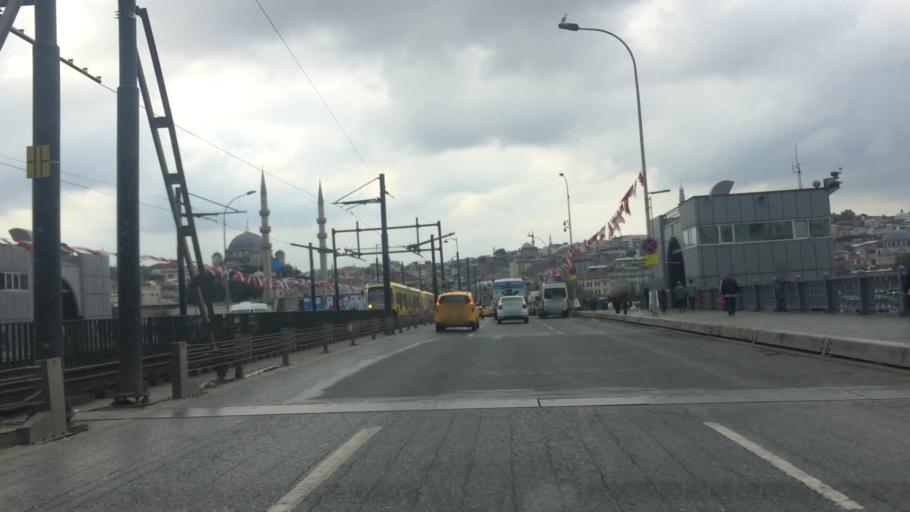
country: TR
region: Istanbul
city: Eminoenue
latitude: 41.0202
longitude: 28.9732
